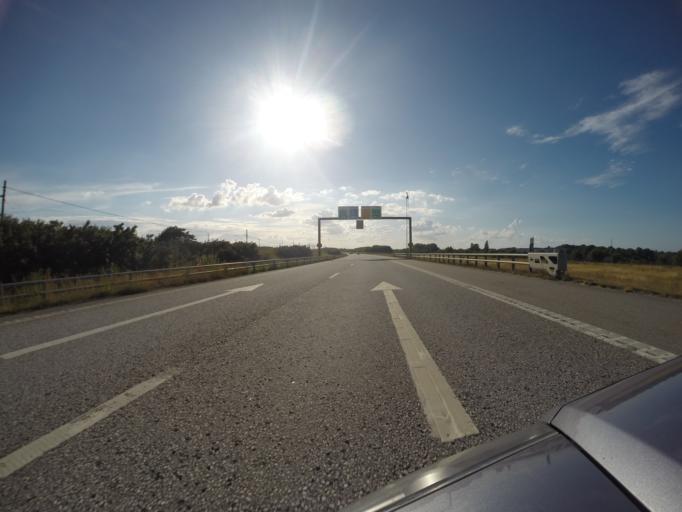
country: SE
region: Skane
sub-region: Malmo
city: Bunkeflostrand
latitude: 55.5642
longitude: 12.9280
